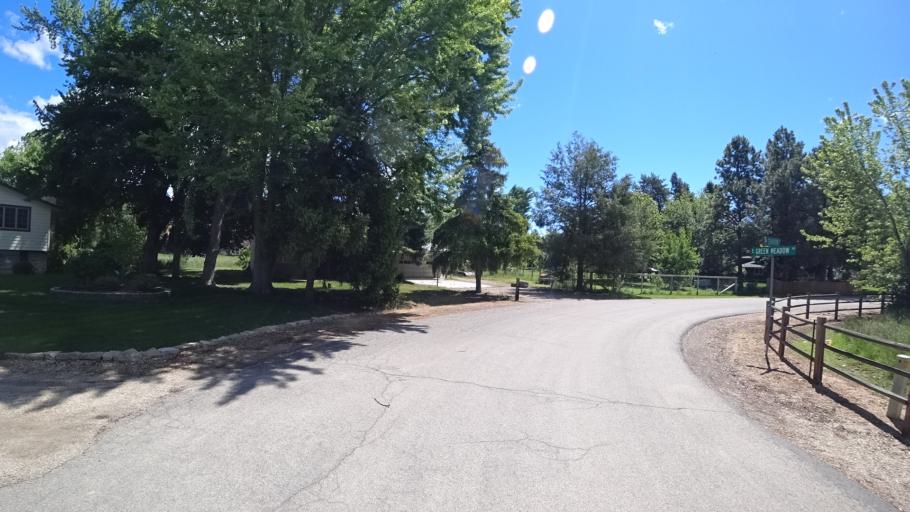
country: US
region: Idaho
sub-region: Ada County
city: Meridian
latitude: 43.6257
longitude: -116.3404
